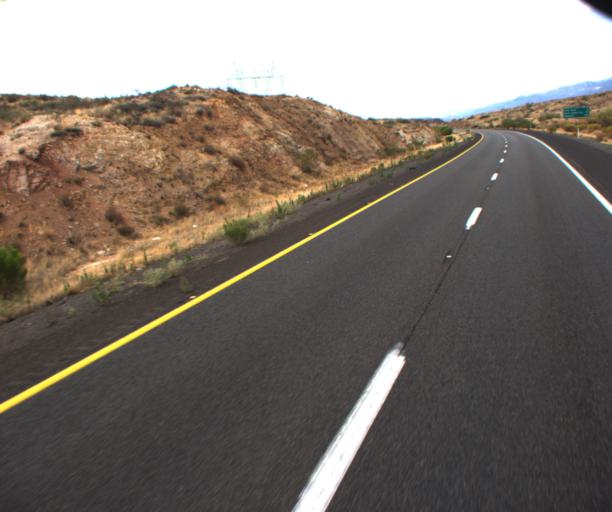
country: US
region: Arizona
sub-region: Yavapai County
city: Cordes Lakes
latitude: 34.2660
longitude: -112.1160
